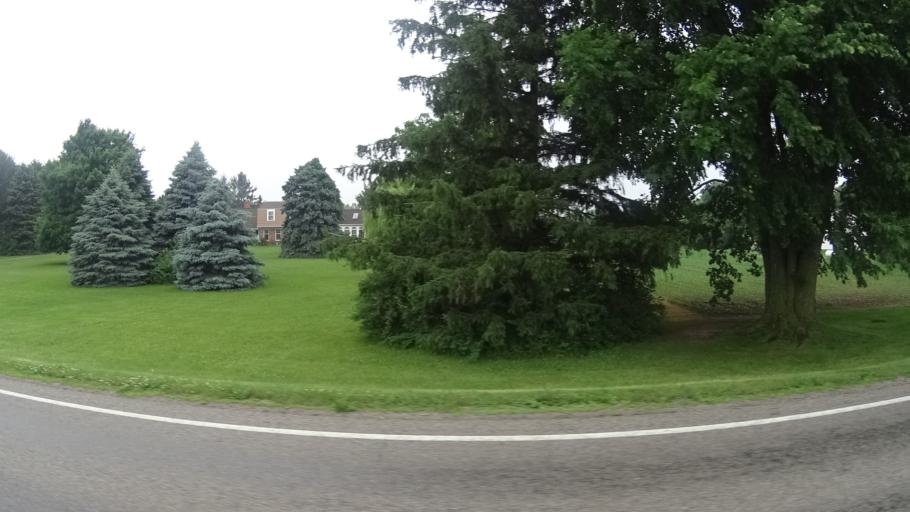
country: US
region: Ohio
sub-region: Huron County
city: Bellevue
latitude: 41.3624
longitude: -82.8233
